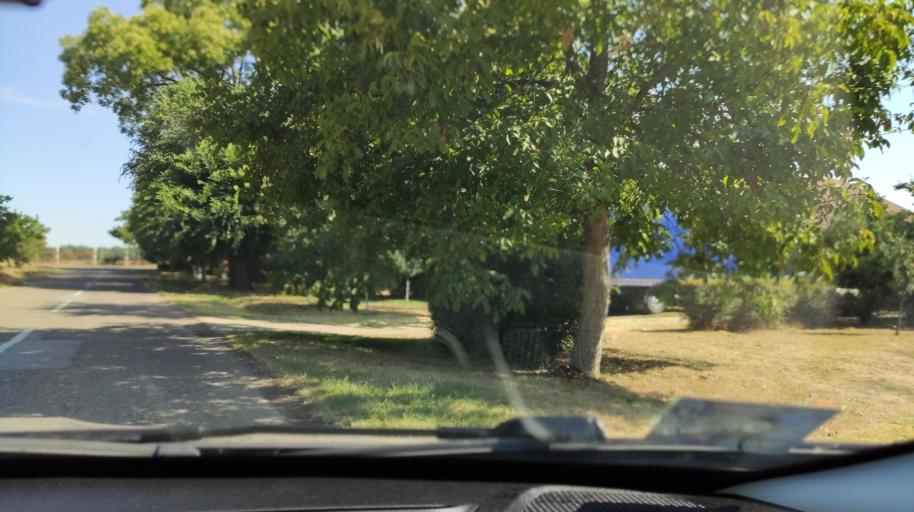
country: RS
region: Autonomna Pokrajina Vojvodina
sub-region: Severnobacki Okrug
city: Backa Topola
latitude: 45.8229
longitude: 19.6228
